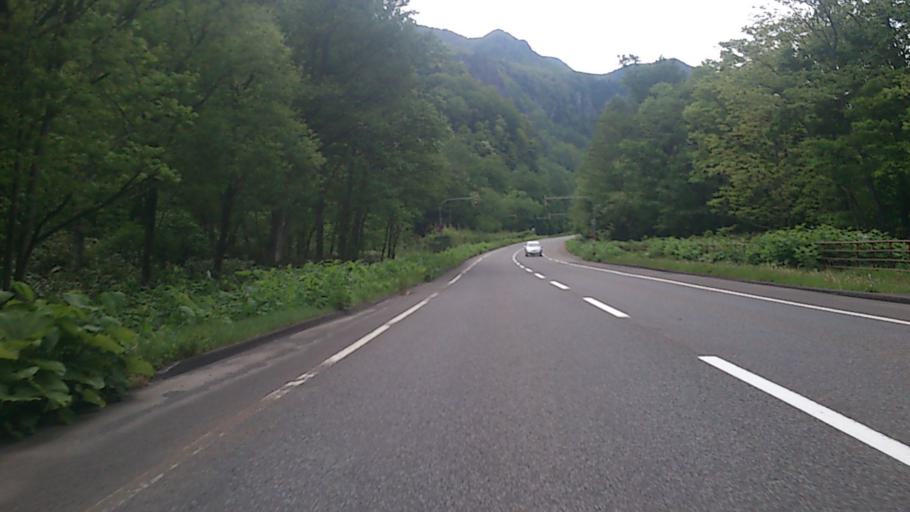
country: JP
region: Hokkaido
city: Kamikawa
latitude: 43.7573
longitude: 142.9239
